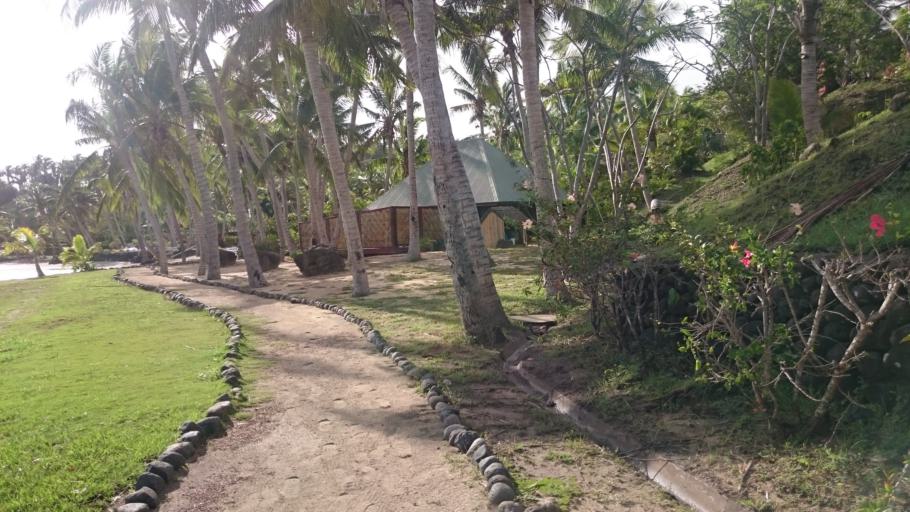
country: FJ
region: Western
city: Ba
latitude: -17.3189
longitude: 178.2050
